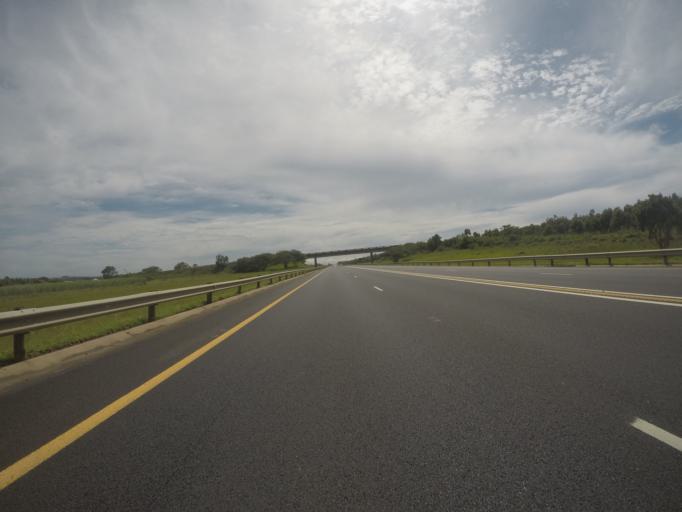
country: ZA
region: KwaZulu-Natal
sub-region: iLembe District Municipality
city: Mandeni
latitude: -29.1548
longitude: 31.5397
